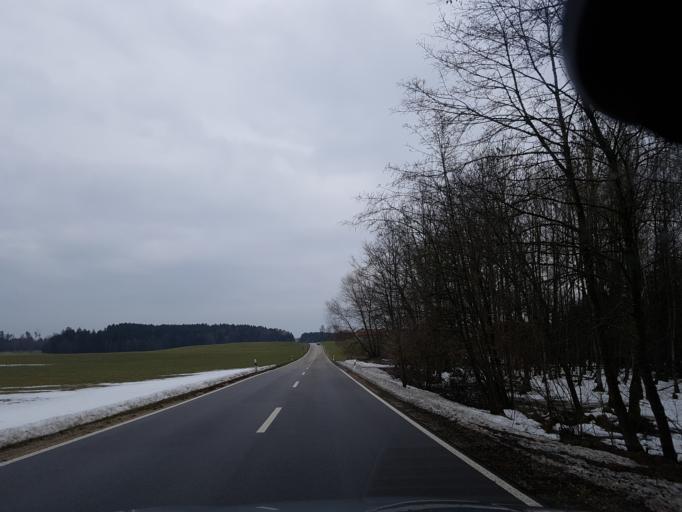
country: DE
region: Bavaria
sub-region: Upper Bavaria
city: Feldkirchen-Westerham
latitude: 47.9413
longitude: 11.8142
